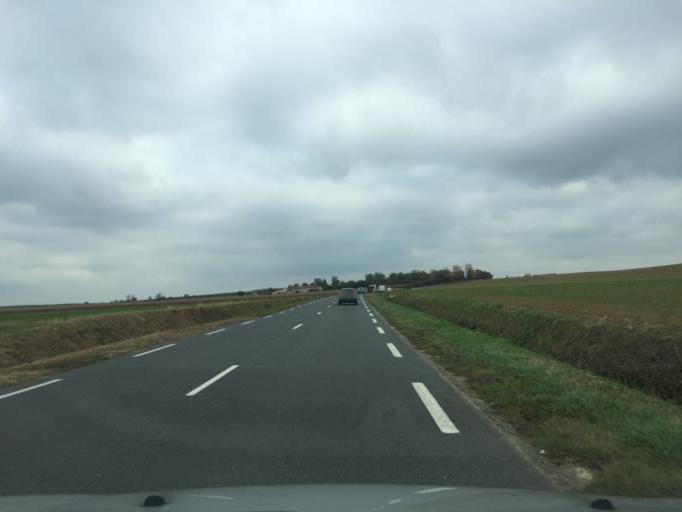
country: FR
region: Rhone-Alpes
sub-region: Departement de l'Ain
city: Reyrieux
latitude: 45.9381
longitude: 4.8463
